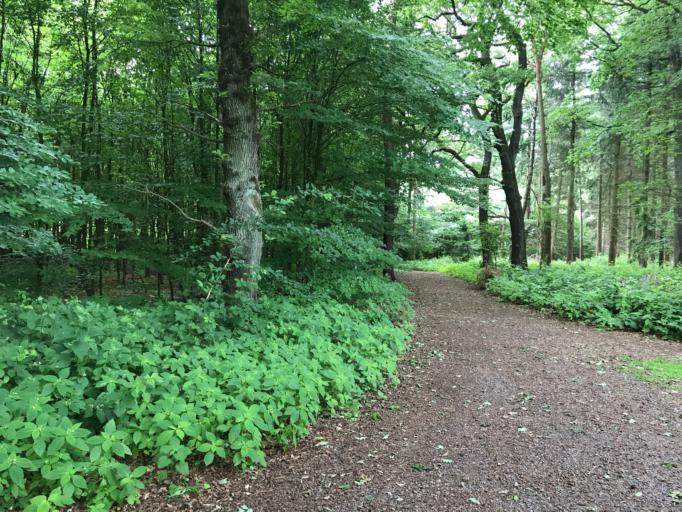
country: DE
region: North Rhine-Westphalia
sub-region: Regierungsbezirk Dusseldorf
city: Duisburg
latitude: 51.4225
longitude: 6.8203
